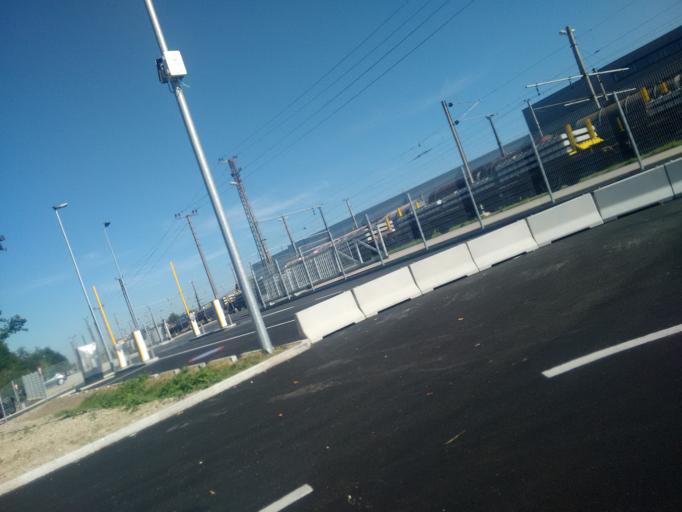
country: AT
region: Upper Austria
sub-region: Wels Stadt
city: Wels
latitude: 48.1680
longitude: 14.0309
